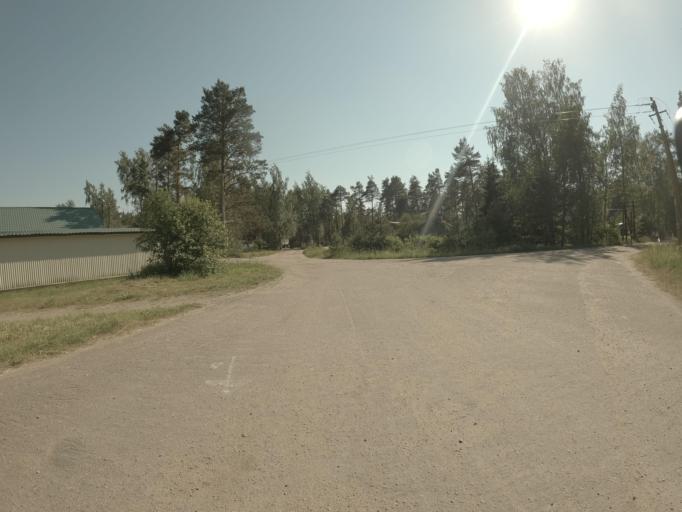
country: RU
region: Leningrad
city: Yakovlevo
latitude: 60.4716
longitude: 29.2771
